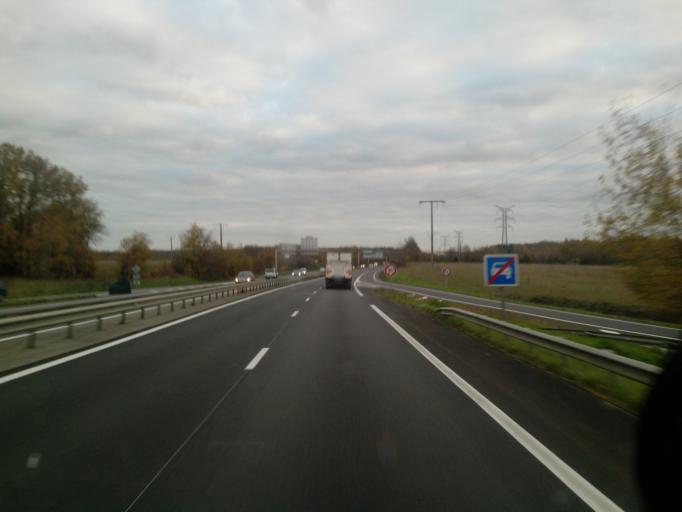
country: FR
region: Poitou-Charentes
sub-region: Departement de la Vienne
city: Mignaloux-Beauvoir
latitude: 46.5729
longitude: 0.3983
